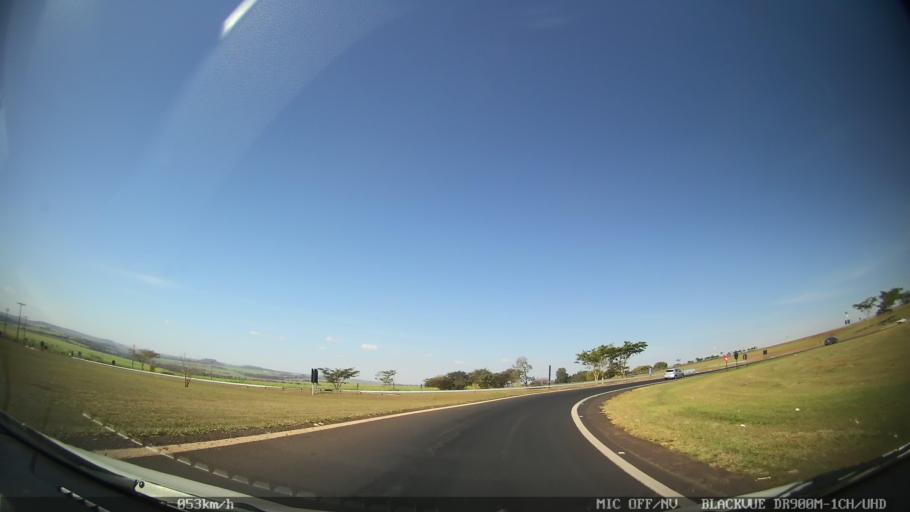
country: BR
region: Sao Paulo
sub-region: Jardinopolis
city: Jardinopolis
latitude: -21.0912
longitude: -47.7943
